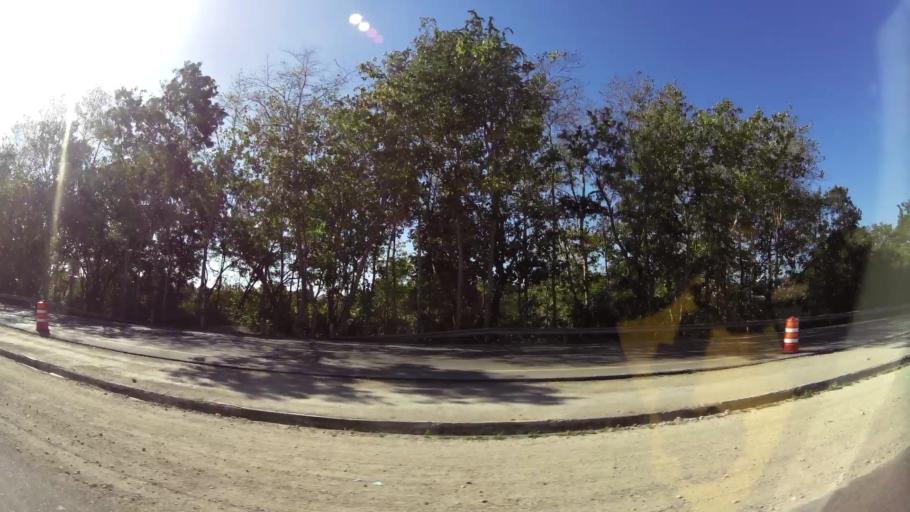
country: DO
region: San Cristobal
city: El Carril
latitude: 18.4380
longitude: -70.0130
